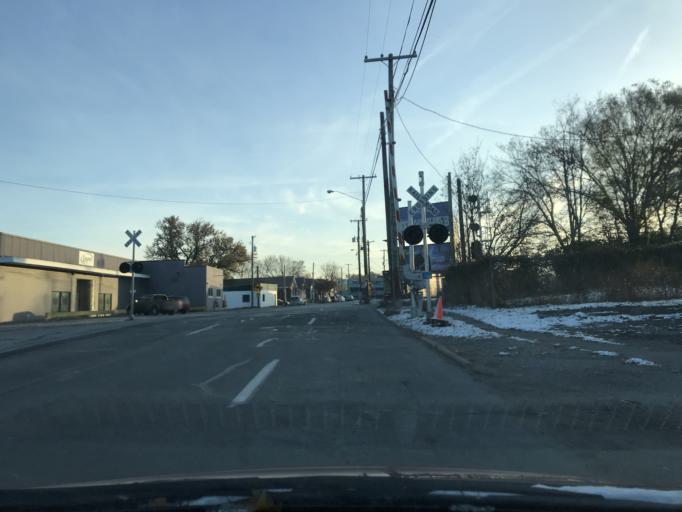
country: US
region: Indiana
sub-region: Clark County
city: Jeffersonville
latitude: 38.2536
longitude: -85.7260
